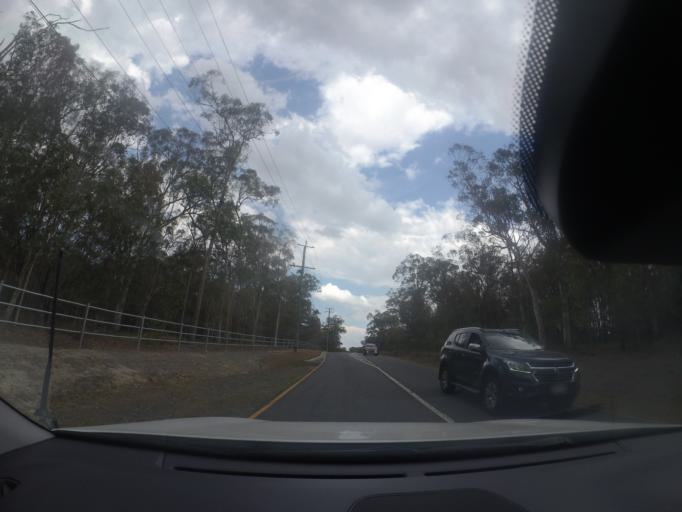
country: AU
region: Queensland
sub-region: Logan
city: Woodridge
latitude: -27.6226
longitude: 153.0937
